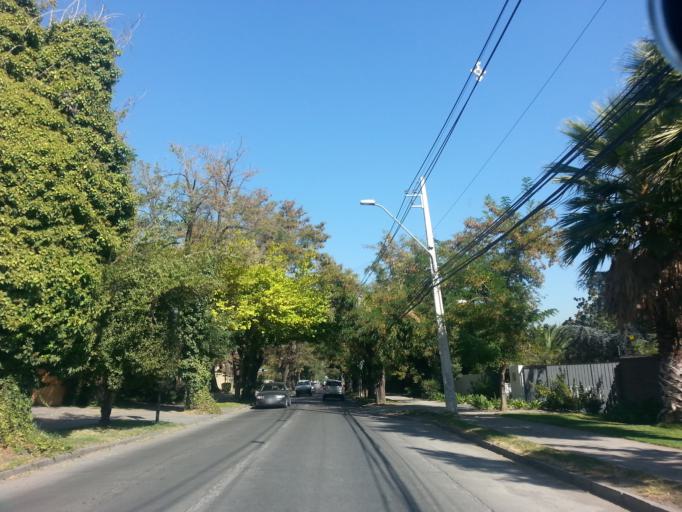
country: CL
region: Santiago Metropolitan
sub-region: Provincia de Santiago
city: Villa Presidente Frei, Nunoa, Santiago, Chile
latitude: -33.4368
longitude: -70.5430
